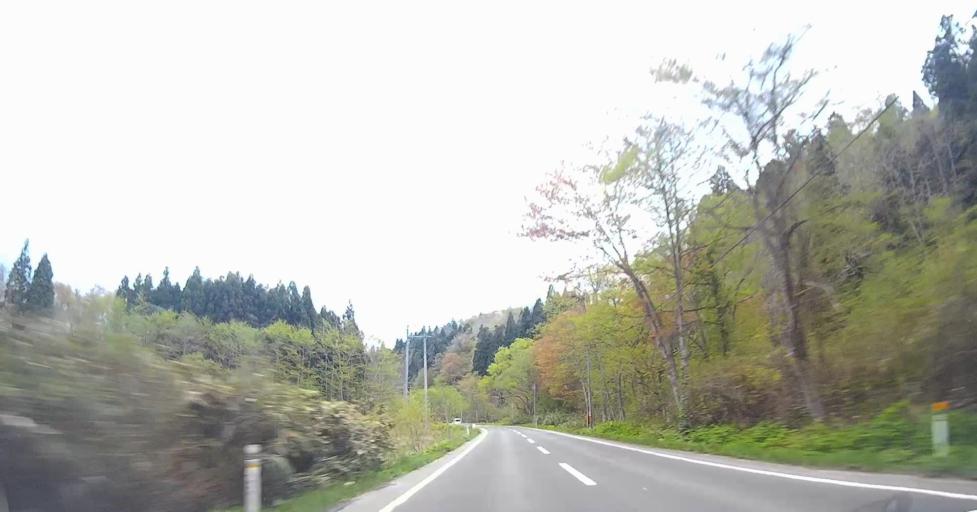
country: JP
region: Aomori
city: Goshogawara
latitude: 41.1265
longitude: 140.5196
